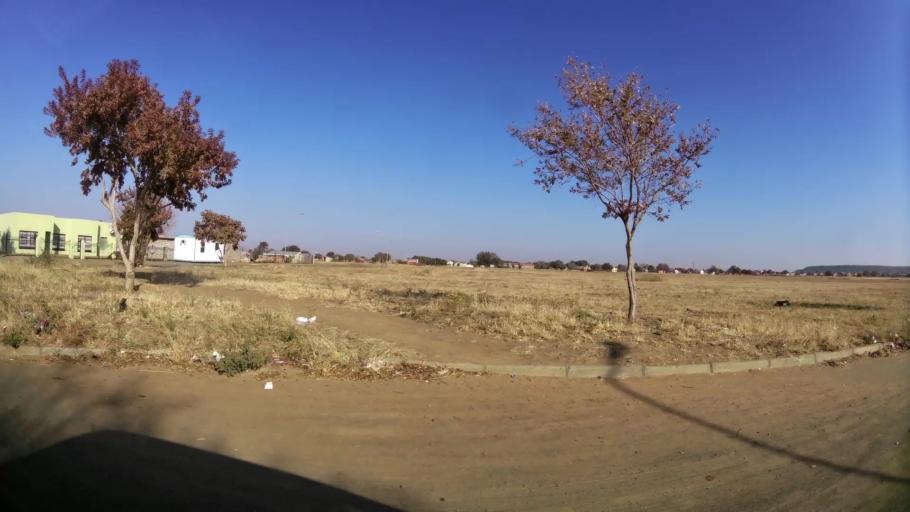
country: ZA
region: Orange Free State
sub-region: Mangaung Metropolitan Municipality
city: Bloemfontein
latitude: -29.1837
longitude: 26.1799
